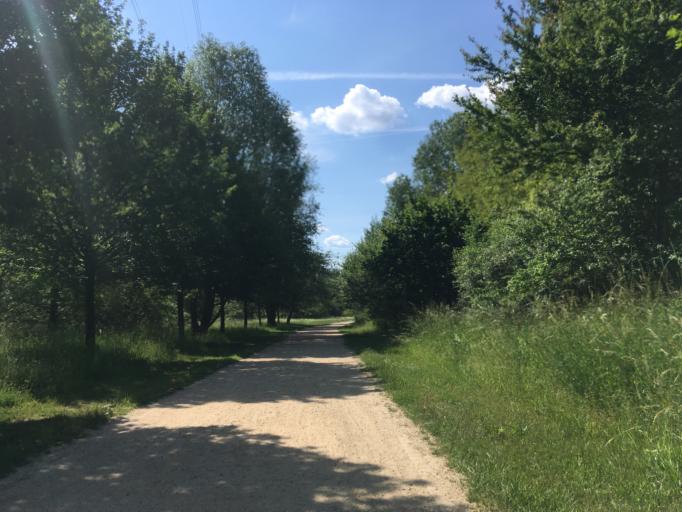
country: DE
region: Berlin
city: Marzahn
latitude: 52.5569
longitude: 13.5860
